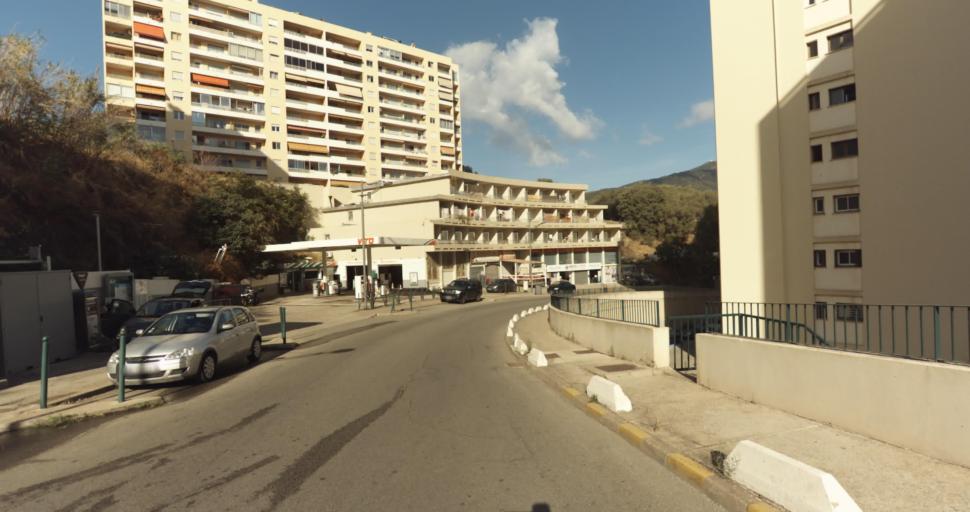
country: FR
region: Corsica
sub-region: Departement de la Corse-du-Sud
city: Ajaccio
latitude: 41.9242
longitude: 8.7347
